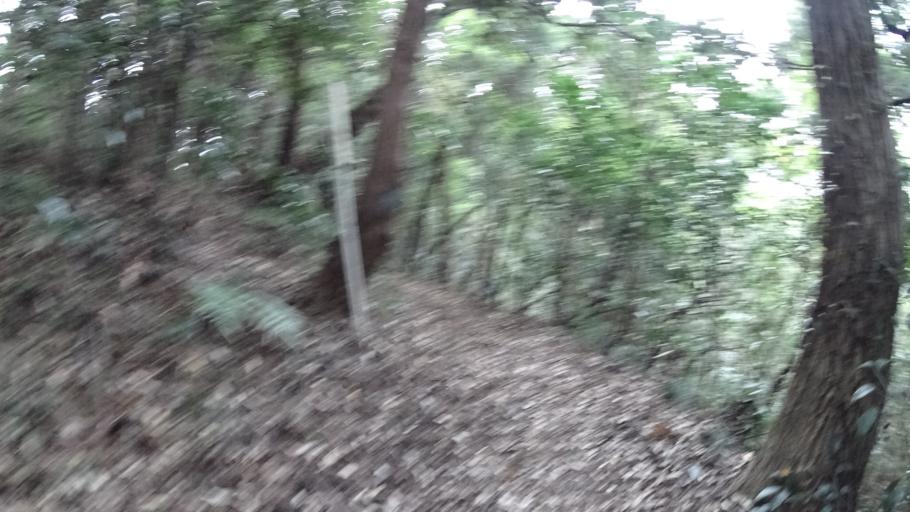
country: JP
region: Kanagawa
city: Zushi
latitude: 35.2901
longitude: 139.6224
